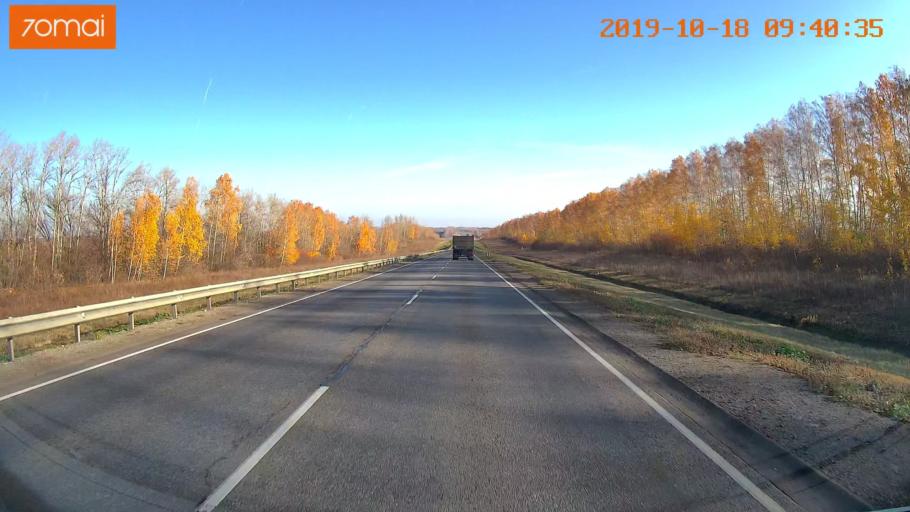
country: RU
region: Tula
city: Kazachka
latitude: 53.2657
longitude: 38.1502
